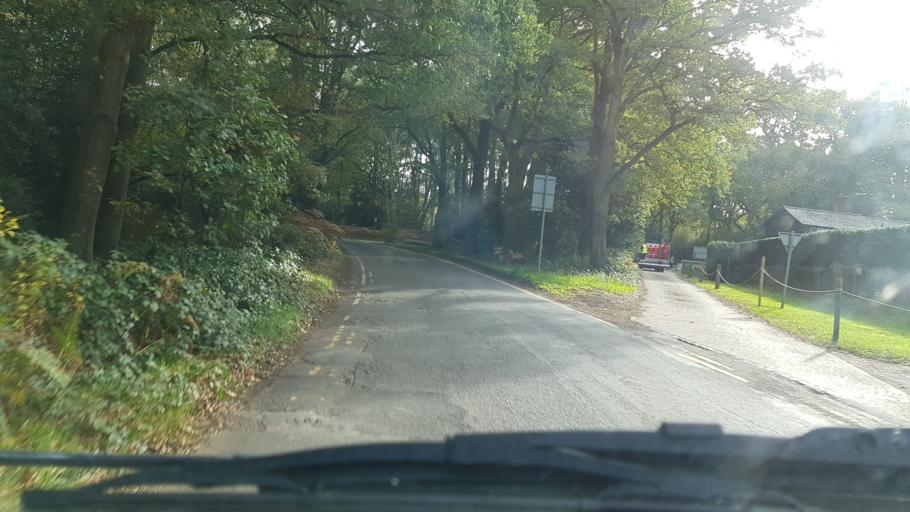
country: GB
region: England
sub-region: Surrey
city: Byfleet
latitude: 51.3192
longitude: -0.4725
